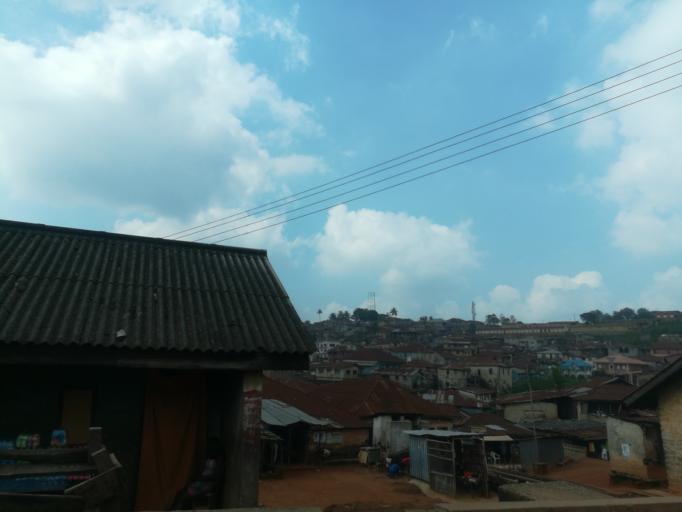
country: NG
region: Oyo
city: Ibadan
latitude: 7.3875
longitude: 3.9012
